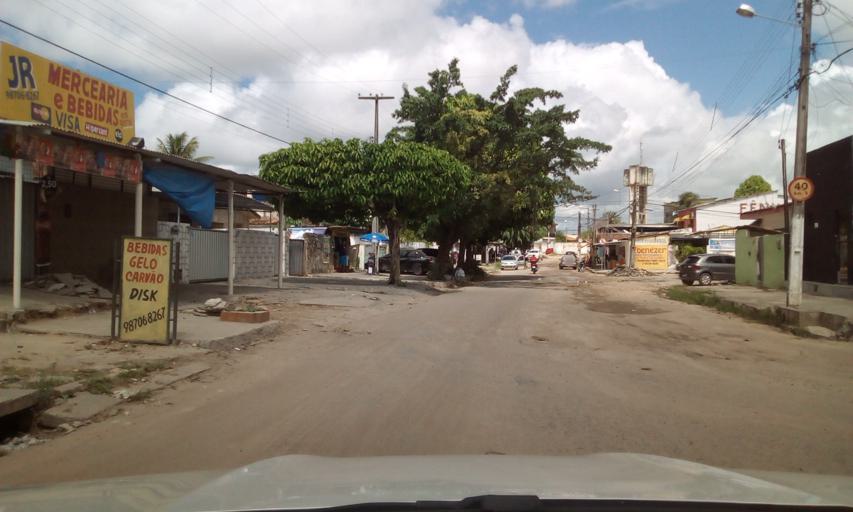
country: BR
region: Paraiba
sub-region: Joao Pessoa
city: Joao Pessoa
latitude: -7.1827
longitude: -34.8696
